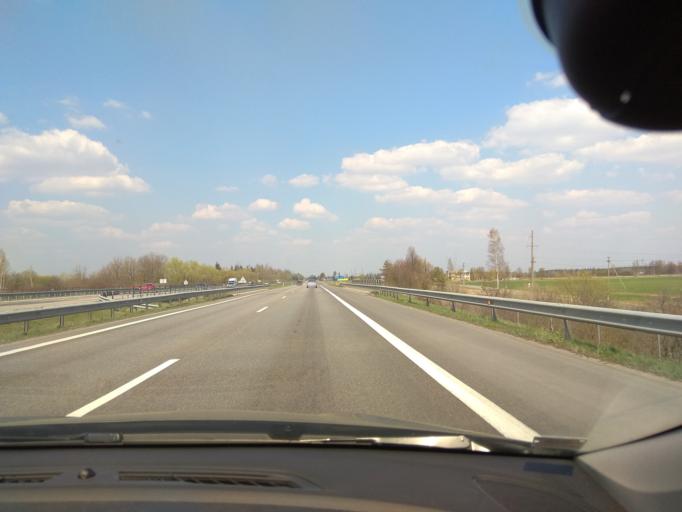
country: LT
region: Kauno apskritis
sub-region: Kaunas
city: Sargenai
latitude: 55.0700
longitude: 23.8154
